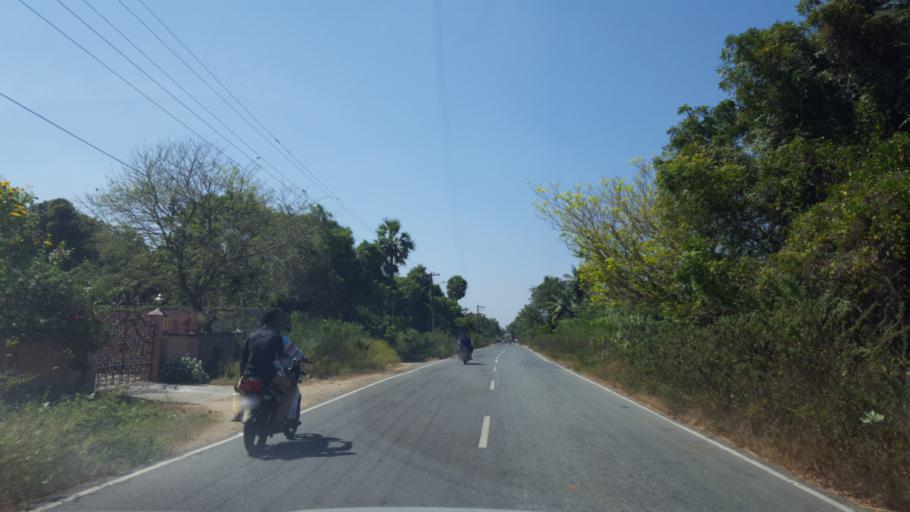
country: IN
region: Tamil Nadu
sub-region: Kancheepuram
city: Wallajahbad
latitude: 12.7659
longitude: 79.9058
